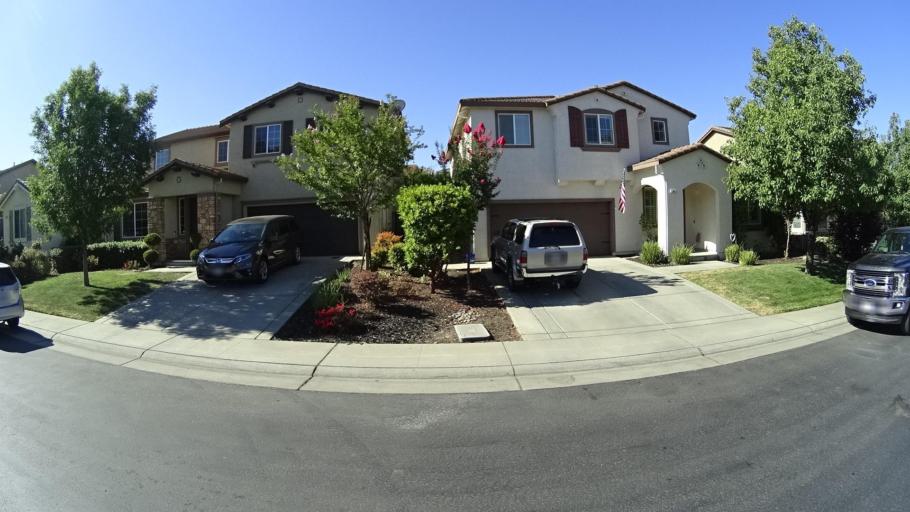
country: US
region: California
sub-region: Placer County
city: Lincoln
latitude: 38.8389
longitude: -121.2845
